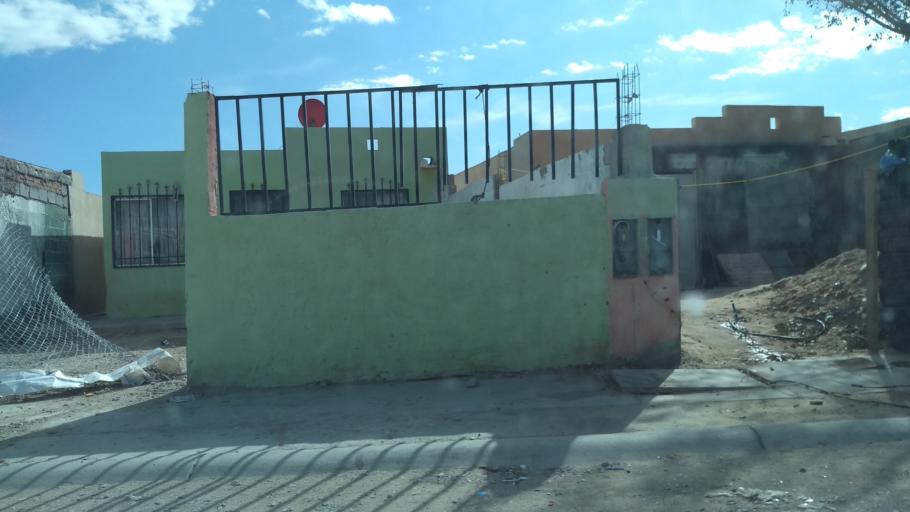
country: US
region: Texas
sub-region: El Paso County
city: San Elizario
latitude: 31.5837
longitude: -106.3528
